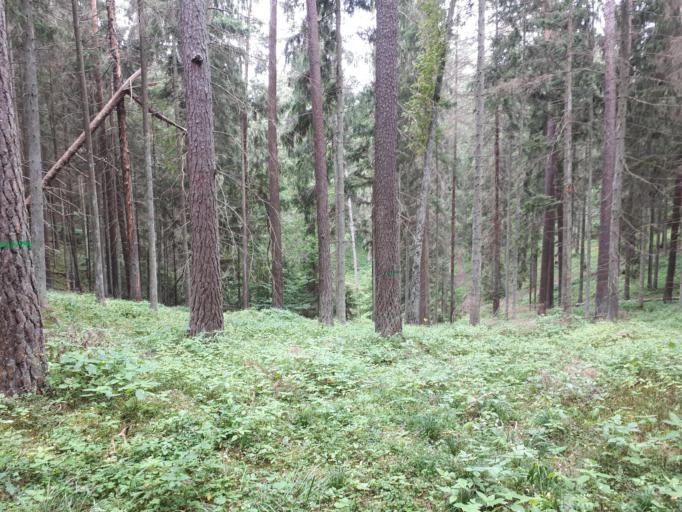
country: LT
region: Vilnius County
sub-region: Trakai
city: Rudiskes
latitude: 54.5848
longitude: 24.6942
